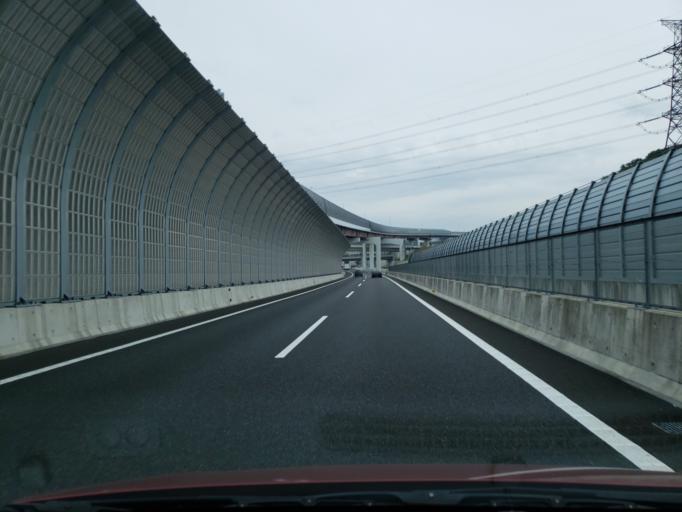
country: JP
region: Hyogo
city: Sandacho
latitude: 34.8497
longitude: 135.2182
